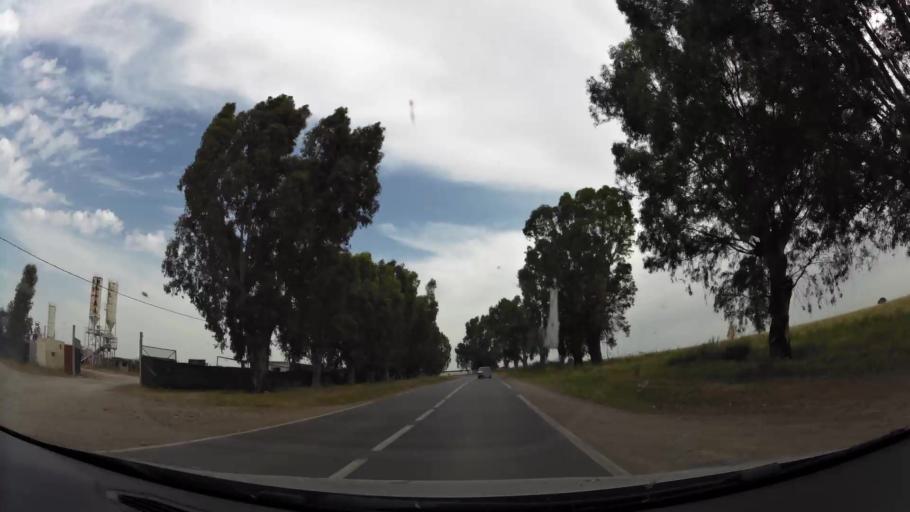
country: MA
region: Rabat-Sale-Zemmour-Zaer
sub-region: Khemisset
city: Tiflet
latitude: 33.8750
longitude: -6.2801
